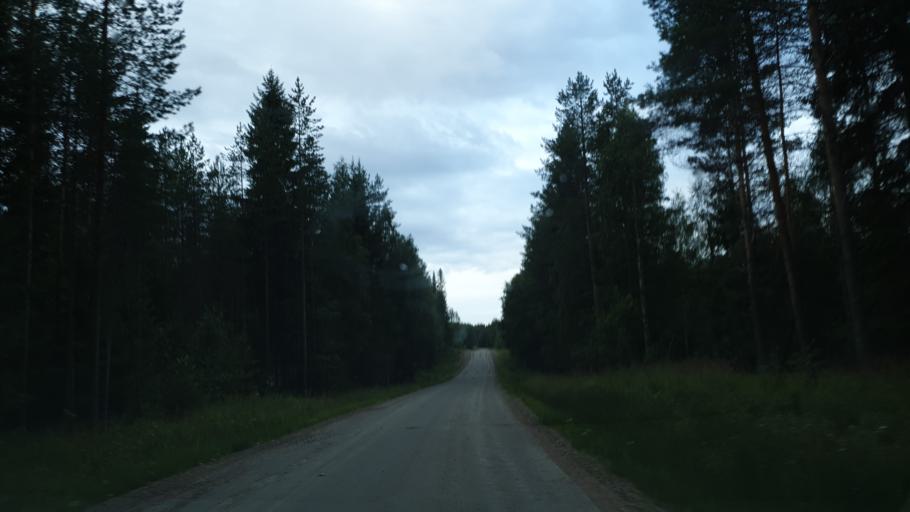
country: FI
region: Kainuu
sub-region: Kehys-Kainuu
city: Kuhmo
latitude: 64.2033
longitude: 29.3730
